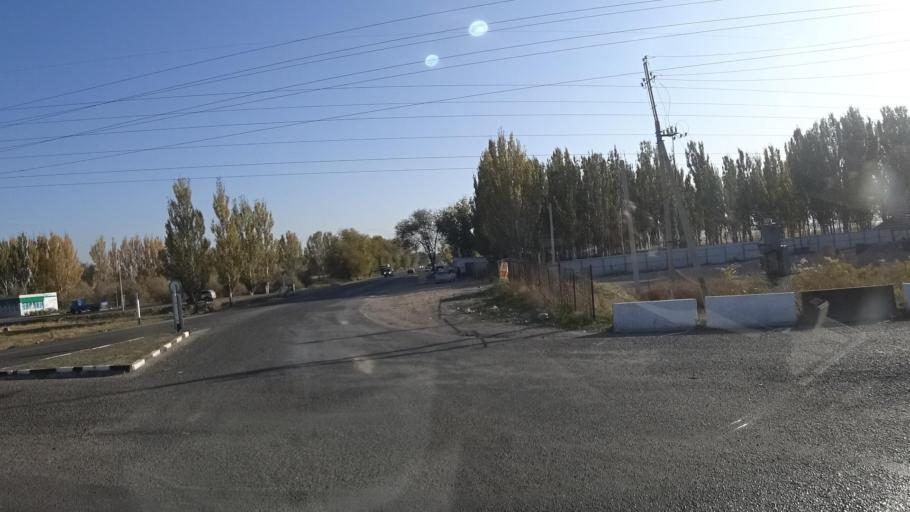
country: KG
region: Chuy
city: Bishkek
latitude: 42.9469
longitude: 74.5666
